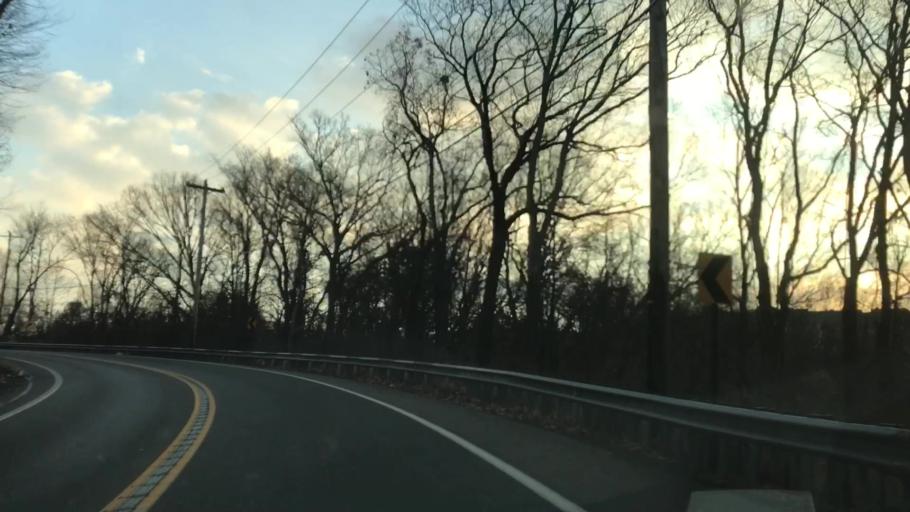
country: US
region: Pennsylvania
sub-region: Allegheny County
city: Carnot-Moon
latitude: 40.5259
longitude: -80.2286
